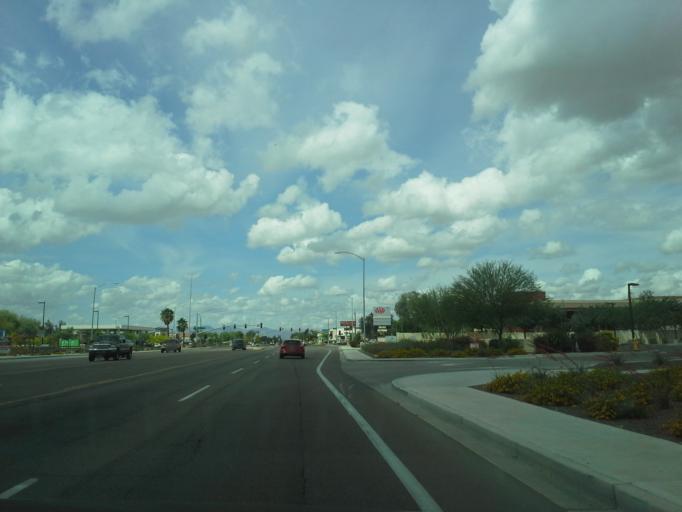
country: US
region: Arizona
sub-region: Maricopa County
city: Peoria
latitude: 33.6104
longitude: -112.2173
